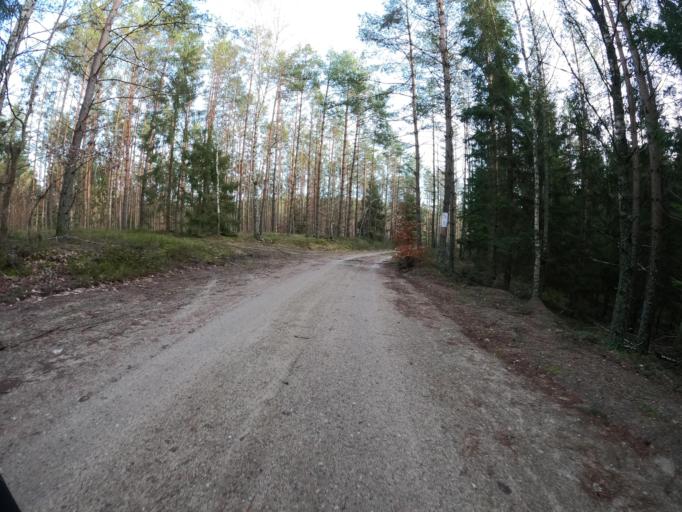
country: PL
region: West Pomeranian Voivodeship
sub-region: Powiat koszalinski
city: Polanow
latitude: 54.1520
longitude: 16.6752
